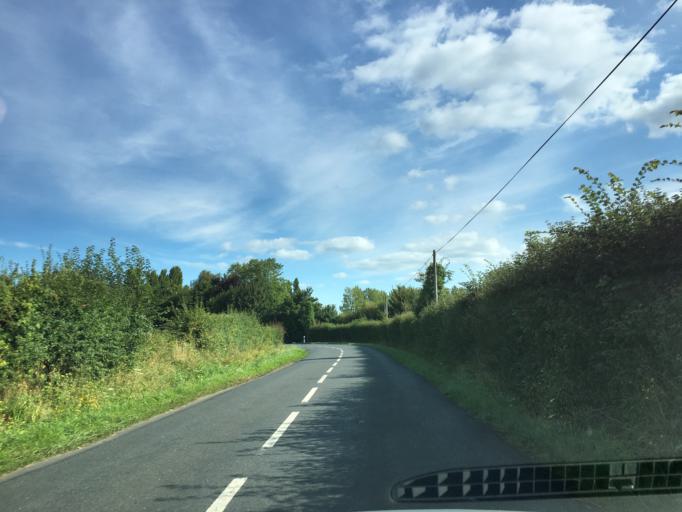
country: FR
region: Lower Normandy
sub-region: Departement du Calvados
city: Cambremer
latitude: 49.1611
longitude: -0.0126
